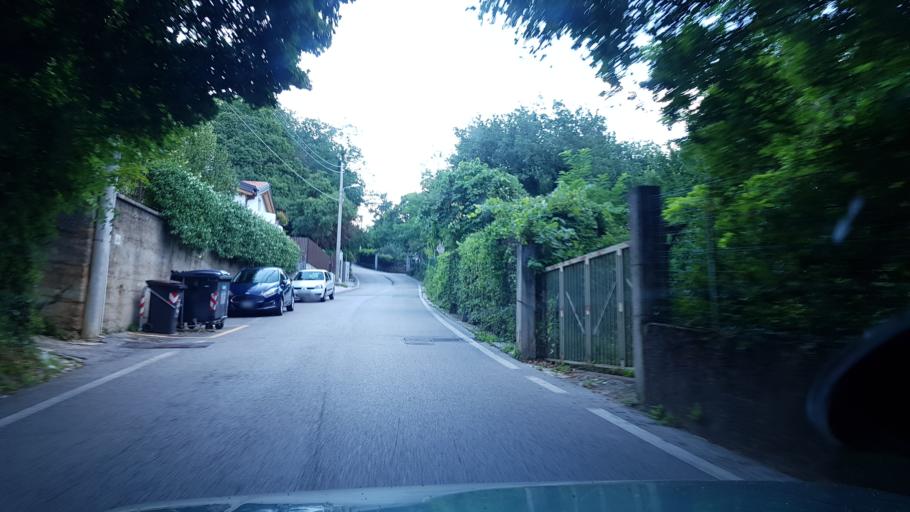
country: IT
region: Friuli Venezia Giulia
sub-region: Provincia di Trieste
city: Trieste
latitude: 45.6465
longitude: 13.8224
